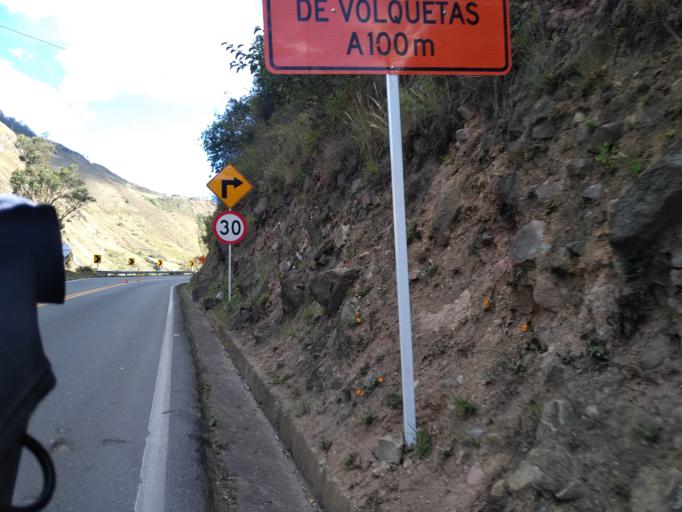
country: CO
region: Narino
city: Funes
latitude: 1.0523
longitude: -77.4506
